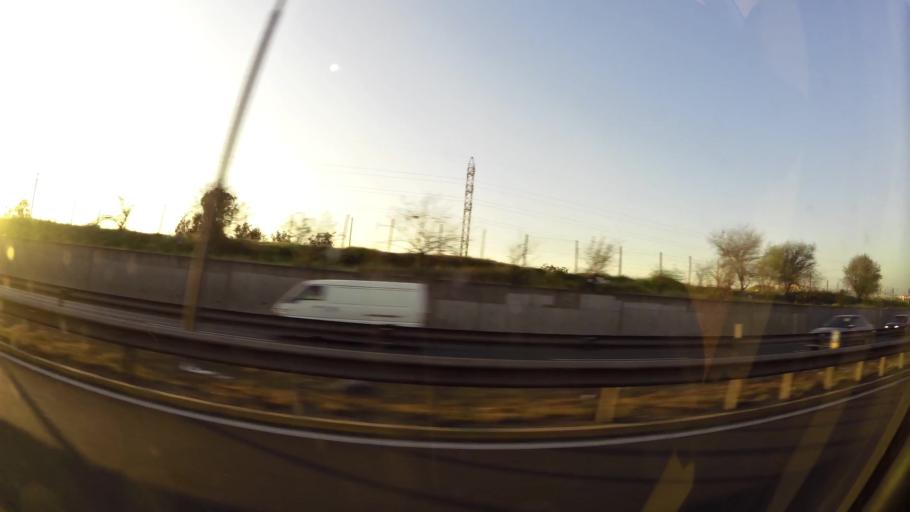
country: CL
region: Santiago Metropolitan
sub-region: Provincia de Santiago
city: Lo Prado
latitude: -33.4798
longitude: -70.6982
